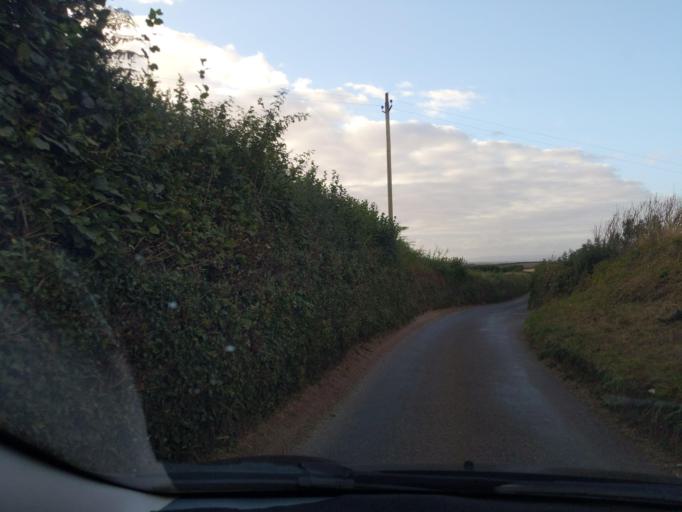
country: GB
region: England
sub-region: Devon
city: Salcombe
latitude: 50.2346
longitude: -3.8192
